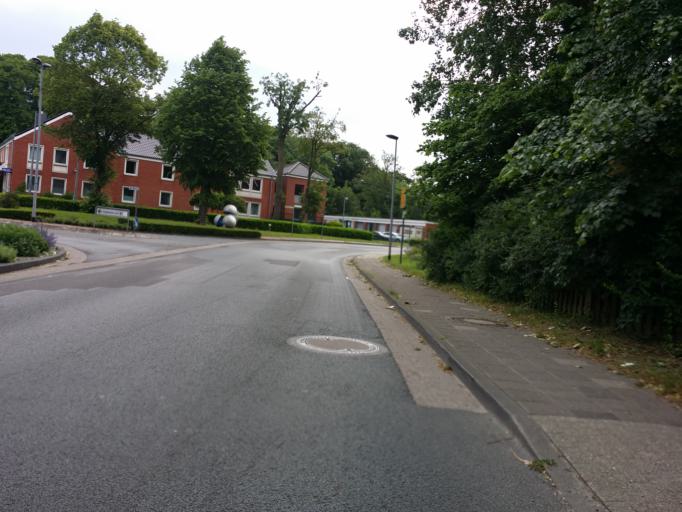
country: DE
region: Lower Saxony
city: Wittmund
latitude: 53.5734
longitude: 7.7819
